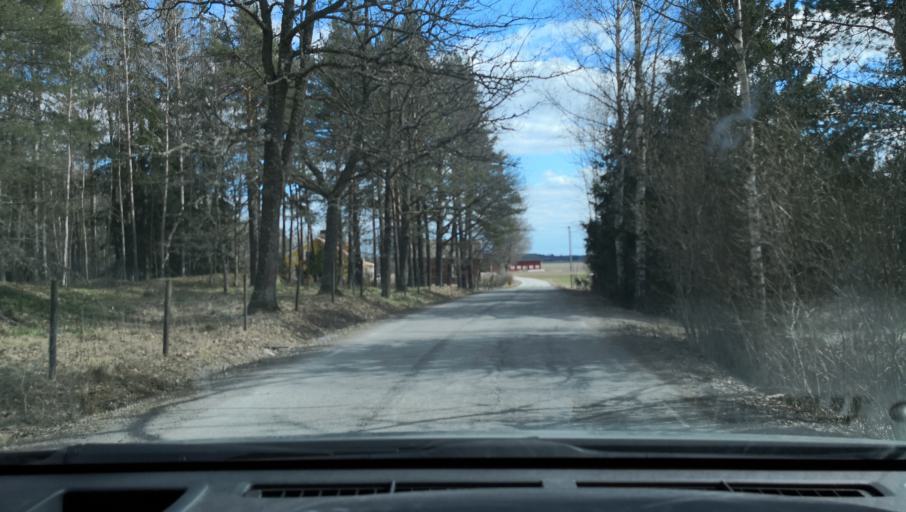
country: SE
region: Vaestmanland
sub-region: Sala Kommun
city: Sala
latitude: 59.8609
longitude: 16.6006
